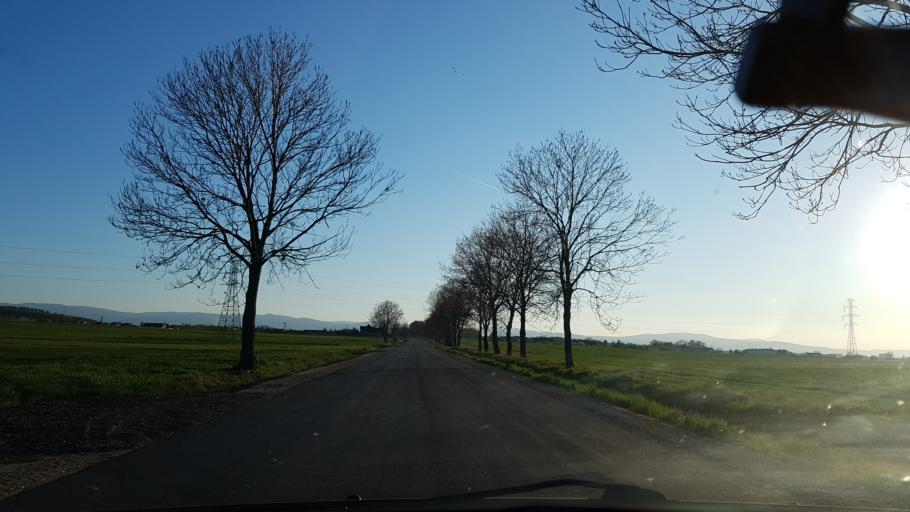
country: CZ
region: Olomoucky
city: Vidnava
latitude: 50.4257
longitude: 17.2383
